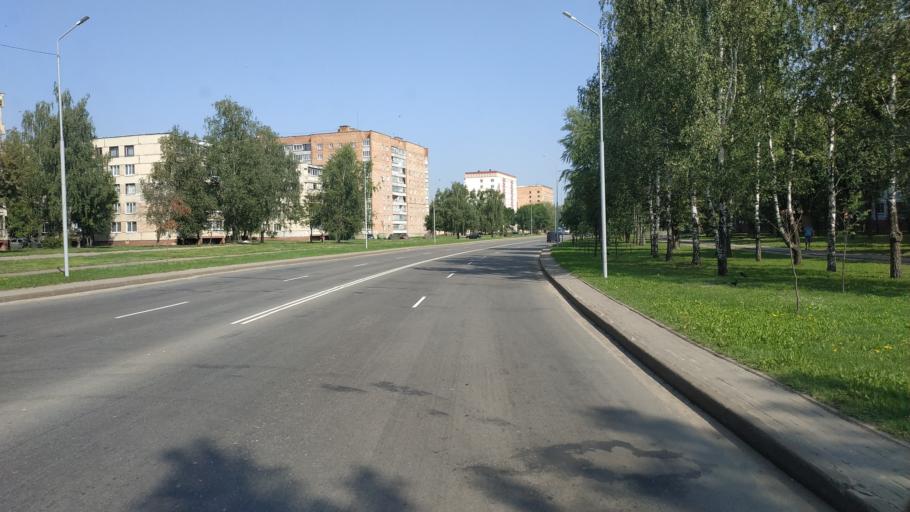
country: BY
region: Mogilev
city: Buynichy
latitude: 53.8673
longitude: 30.3146
